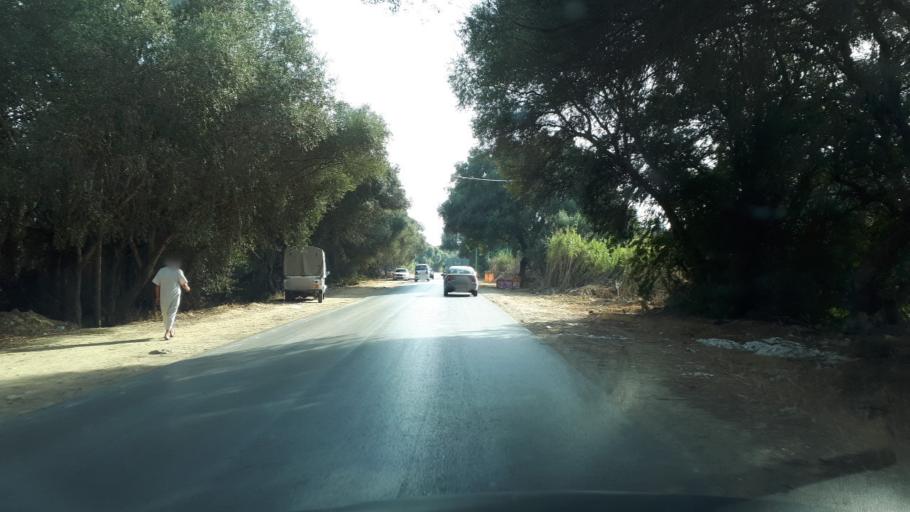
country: DZ
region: Tipaza
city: Zeralda
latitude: 36.7317
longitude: 2.9001
